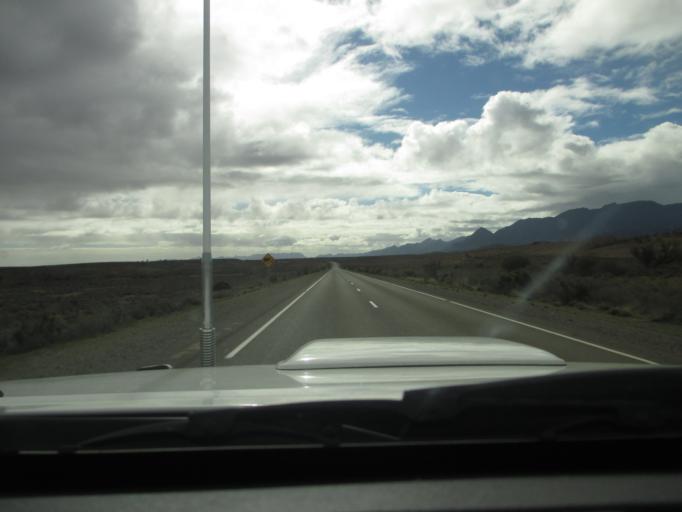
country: AU
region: South Australia
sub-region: Flinders Ranges
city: Quorn
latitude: -31.5727
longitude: 138.4231
